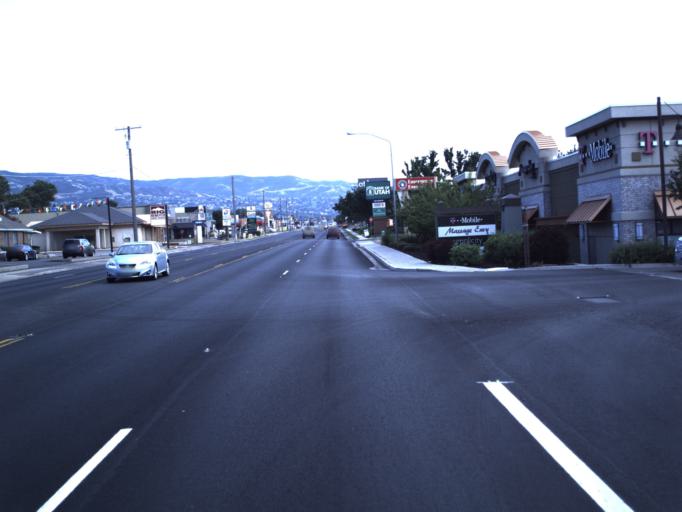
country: US
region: Utah
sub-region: Davis County
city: West Bountiful
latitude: 40.8896
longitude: -111.8923
